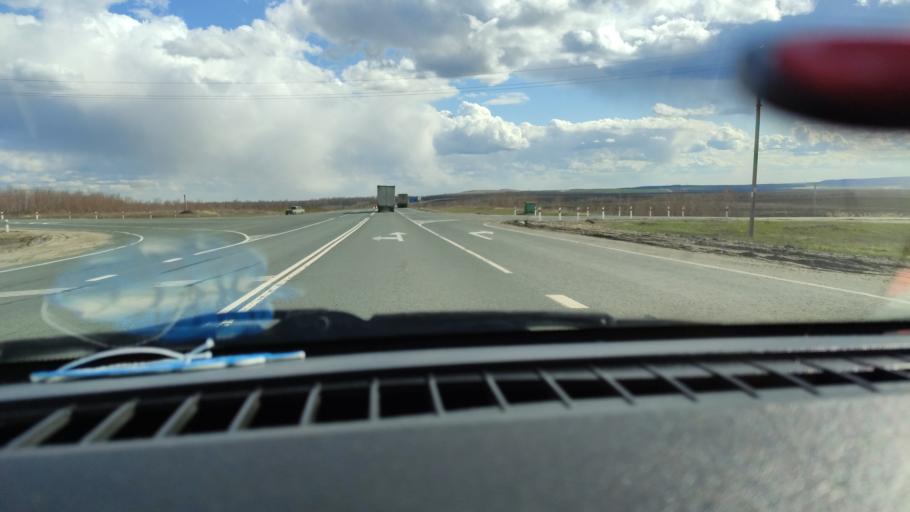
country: RU
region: Saratov
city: Alekseyevka
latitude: 52.2889
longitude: 47.9305
